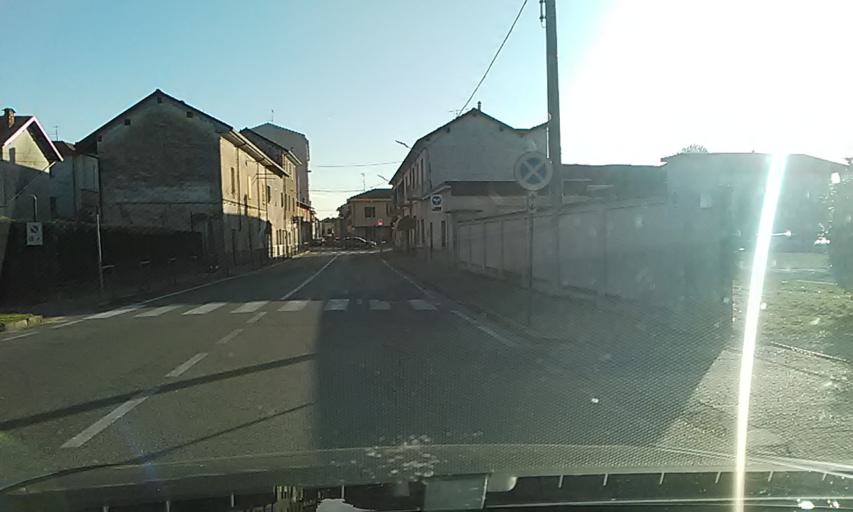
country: IT
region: Piedmont
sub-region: Provincia di Novara
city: Momo
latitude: 45.5742
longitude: 8.5569
